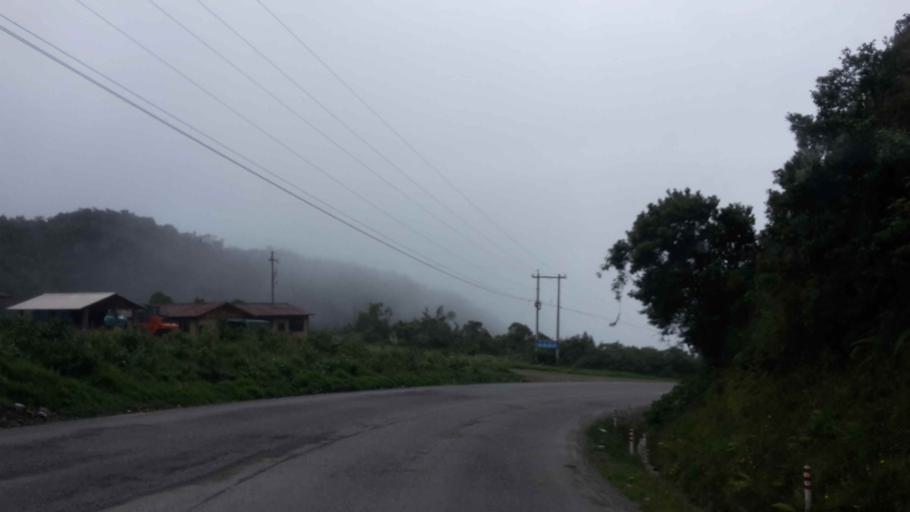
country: BO
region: Cochabamba
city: Colomi
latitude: -17.1851
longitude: -65.8994
